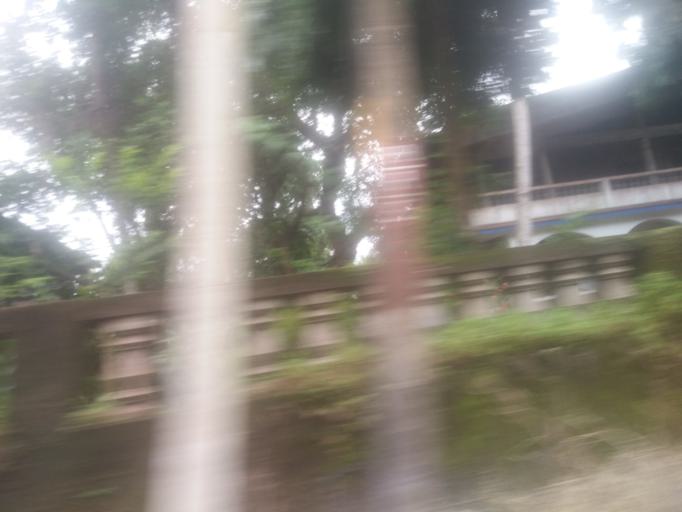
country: IN
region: Goa
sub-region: South Goa
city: Chinchinim
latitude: 15.2128
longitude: 73.9753
